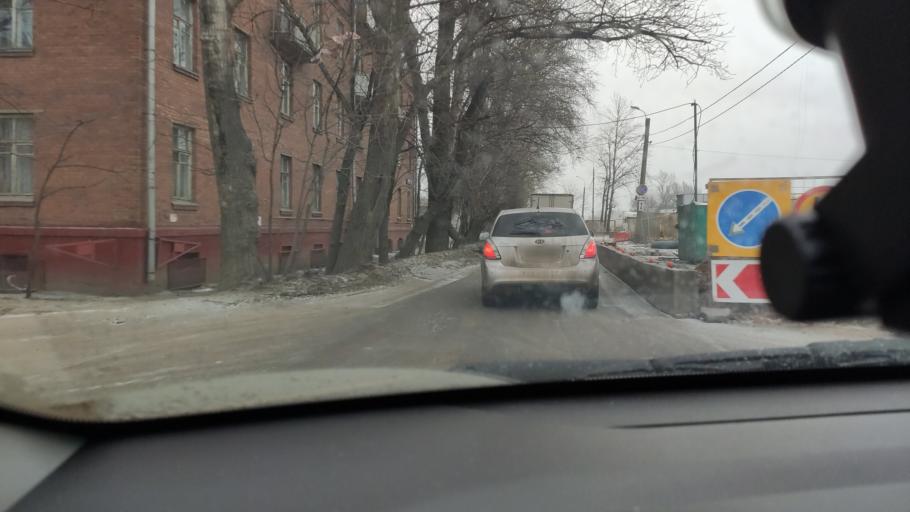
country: RU
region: Moscow
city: Annino
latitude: 55.5858
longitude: 37.6064
